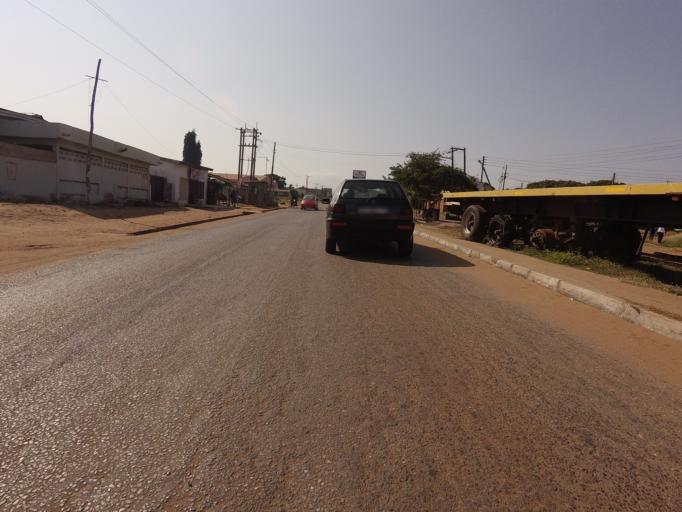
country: GH
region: Greater Accra
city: Teshi Old Town
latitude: 5.5901
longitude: -0.0993
